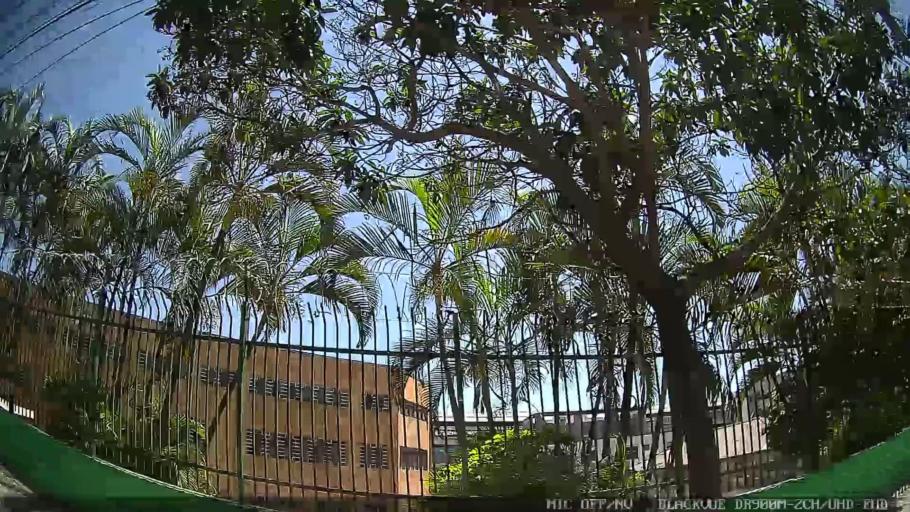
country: BR
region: Sao Paulo
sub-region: Sao Caetano Do Sul
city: Sao Caetano do Sul
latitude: -23.5885
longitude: -46.5434
